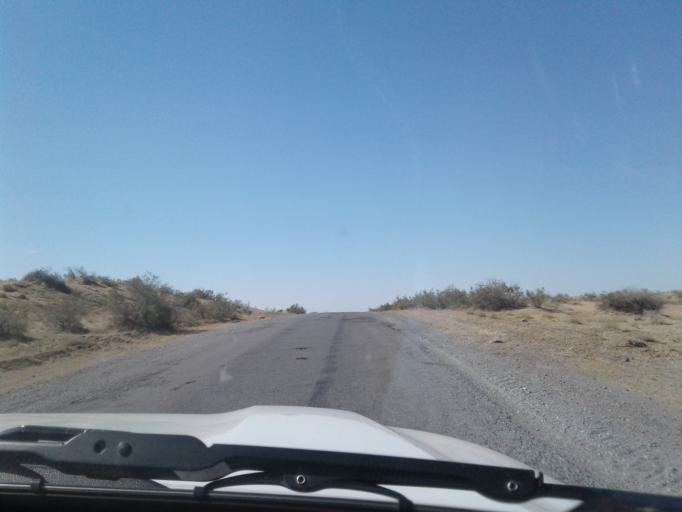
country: AF
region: Badghis
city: Bala Murghab
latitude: 36.2133
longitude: 62.6036
